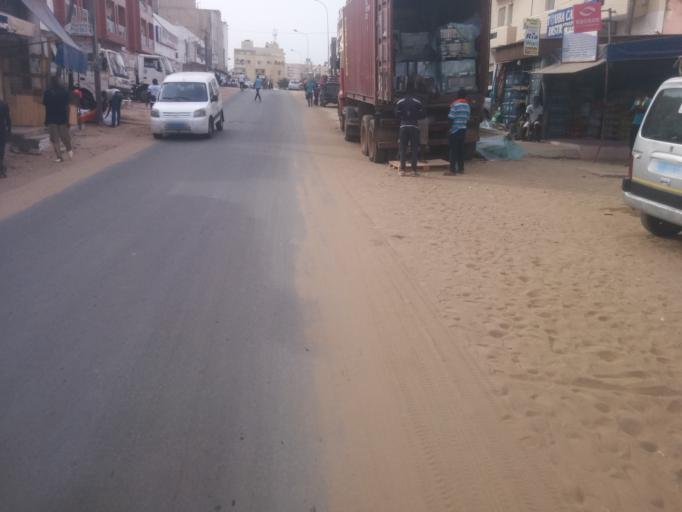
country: SN
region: Dakar
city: Grand Dakar
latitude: 14.7523
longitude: -17.4407
